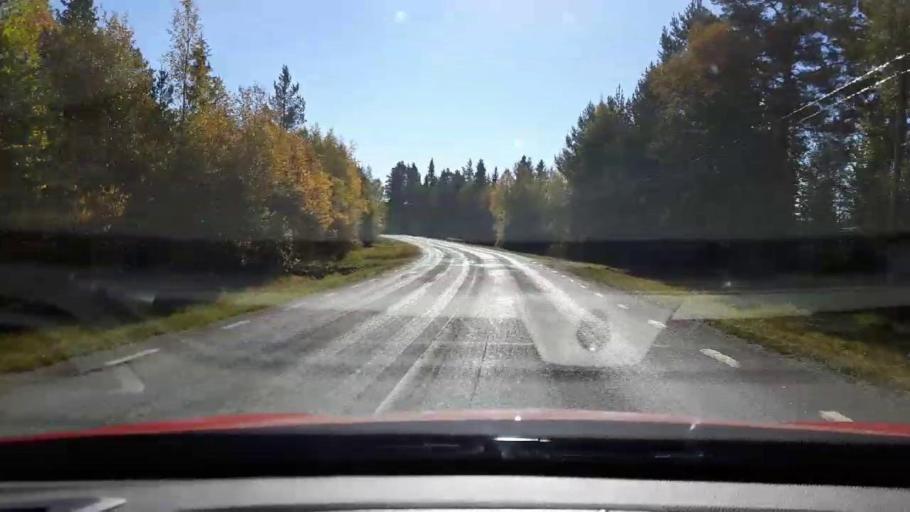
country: SE
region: Jaemtland
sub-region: Harjedalens Kommun
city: Sveg
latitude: 62.3404
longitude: 14.0397
